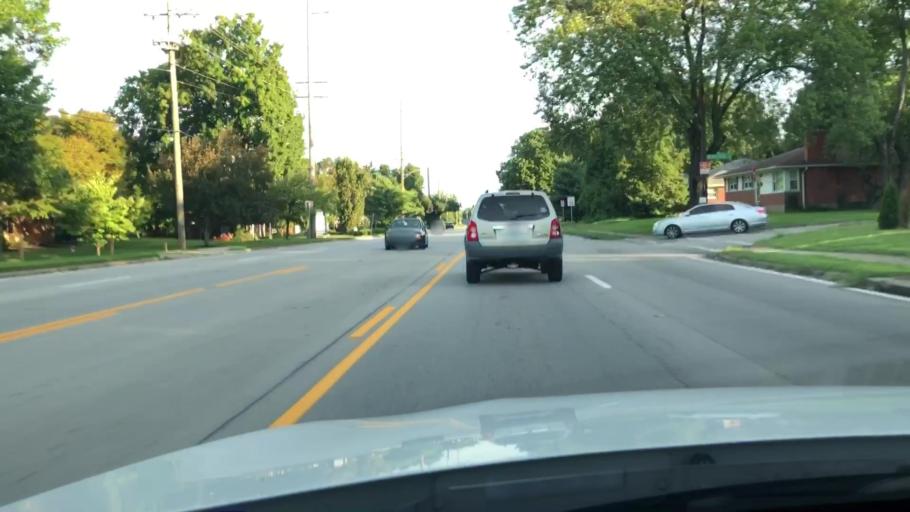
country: US
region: Kentucky
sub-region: Jefferson County
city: Saint Regis Park
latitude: 38.2223
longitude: -85.6325
